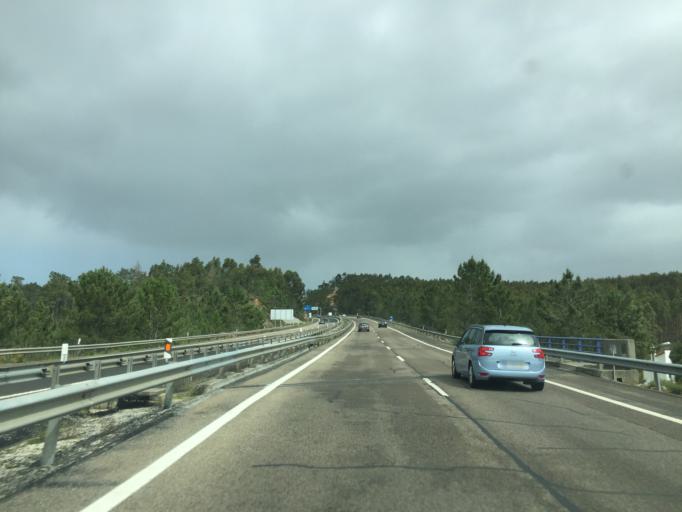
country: PT
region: Lisbon
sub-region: Torres Vedras
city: Torres Vedras
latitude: 39.1029
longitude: -9.2399
